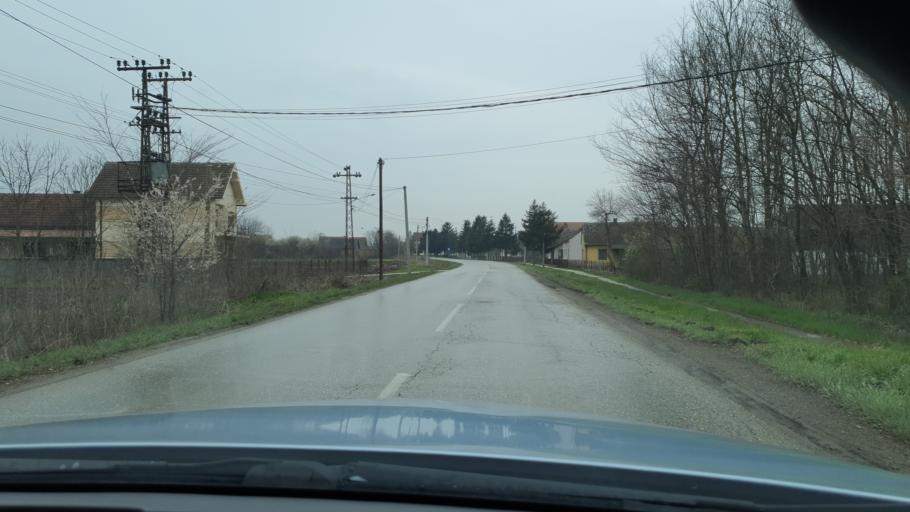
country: RS
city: Stitar
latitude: 44.7897
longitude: 19.5809
